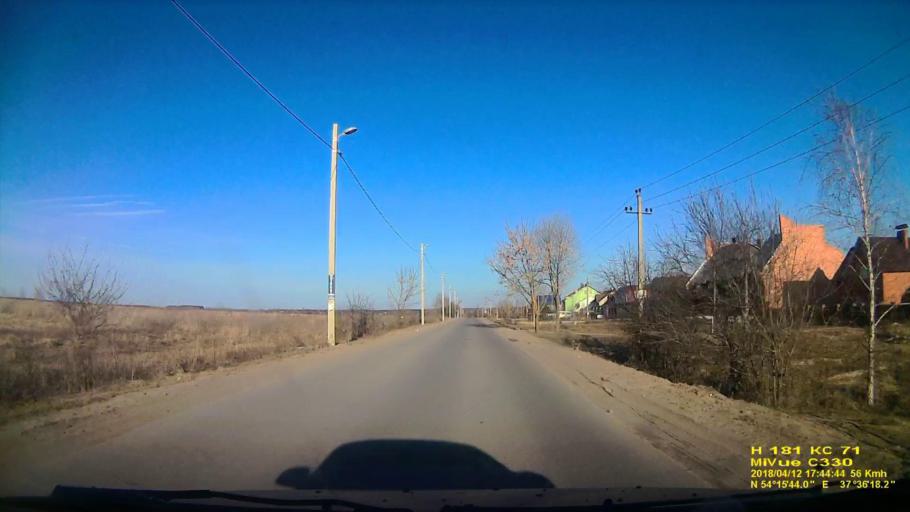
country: RU
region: Tula
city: Gorelki
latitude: 54.2622
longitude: 37.6052
